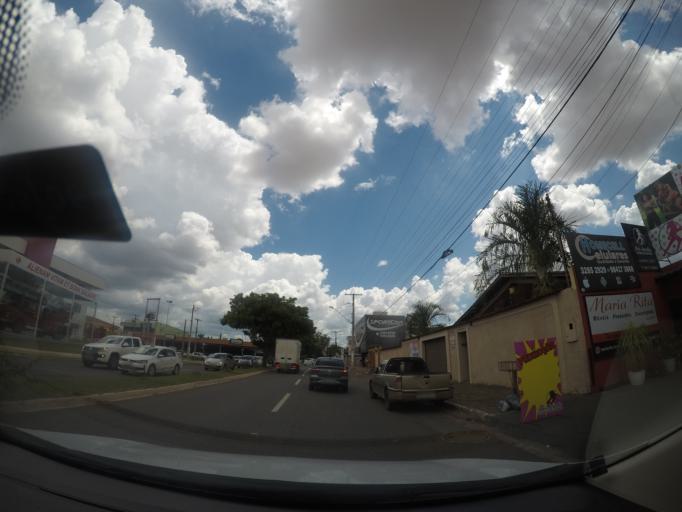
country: BR
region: Goias
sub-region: Goiania
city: Goiania
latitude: -16.7005
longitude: -49.2818
